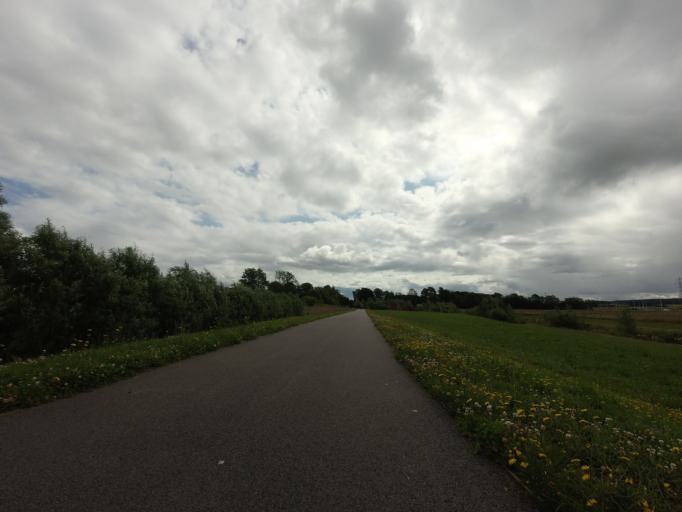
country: GB
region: Scotland
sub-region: Moray
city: Lhanbryd
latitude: 57.6435
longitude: -3.2669
